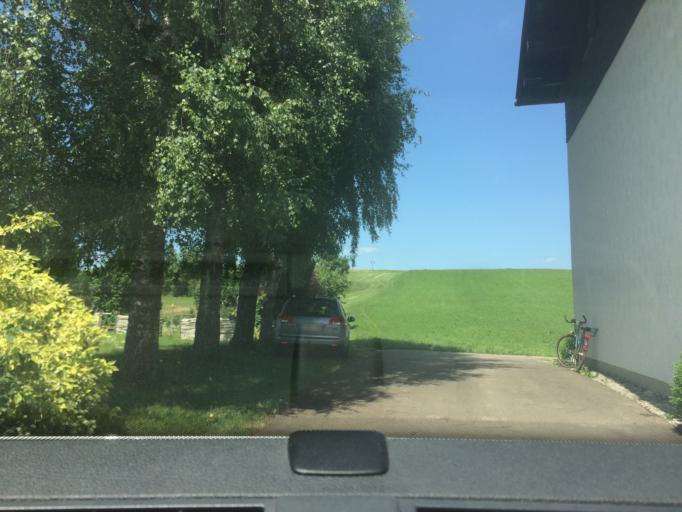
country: DE
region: Bavaria
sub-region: Upper Bavaria
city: Bruckmuhl
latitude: 47.8957
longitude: 11.9157
